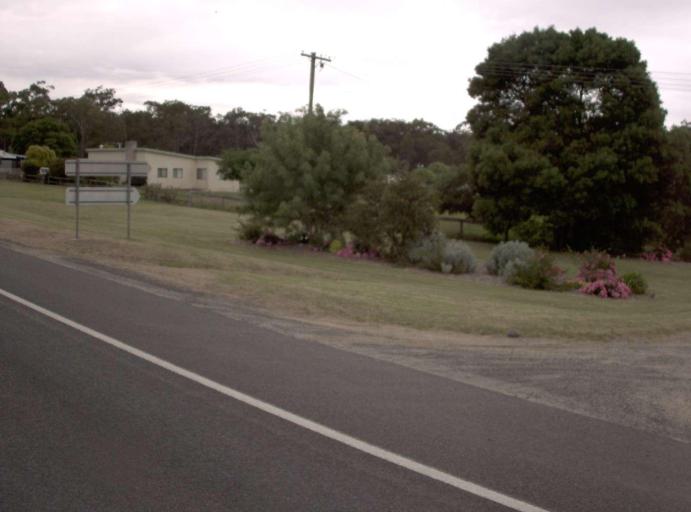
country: AU
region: Victoria
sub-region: Wellington
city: Sale
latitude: -38.5237
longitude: 146.8744
